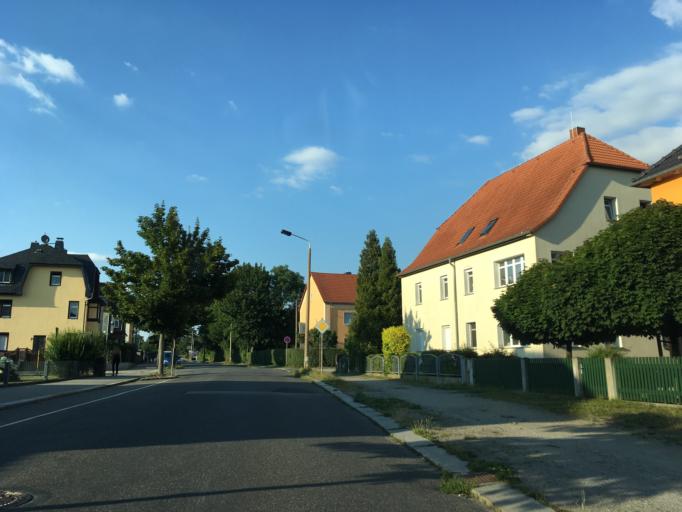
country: DE
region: Saxony
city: Radeberg
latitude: 51.1081
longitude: 13.9178
